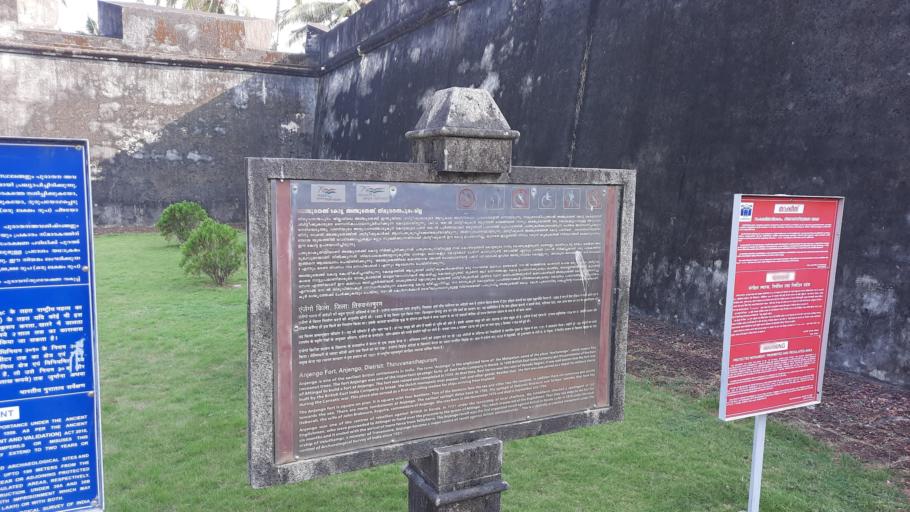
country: IN
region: Kerala
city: Vettur
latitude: 8.6628
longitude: 76.7647
